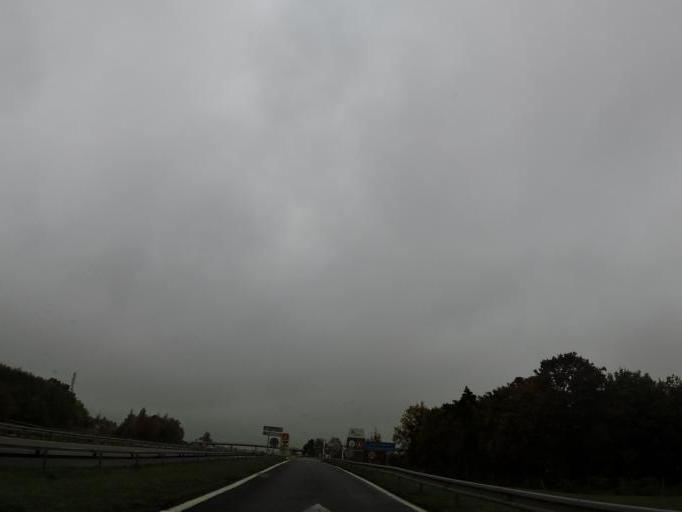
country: FR
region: Champagne-Ardenne
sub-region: Departement de la Marne
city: Verzy
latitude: 49.1172
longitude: 4.2478
